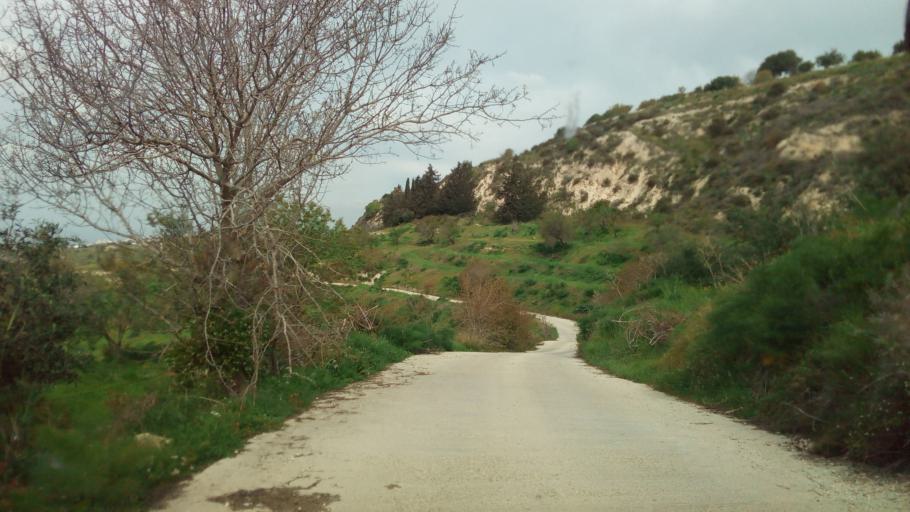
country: CY
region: Pafos
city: Mesogi
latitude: 34.8007
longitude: 32.4767
